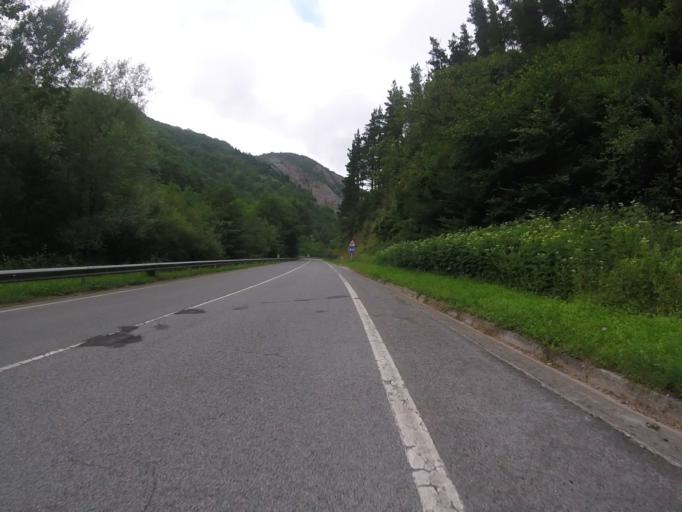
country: ES
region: Navarre
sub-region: Provincia de Navarra
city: Saldias
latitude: 43.1047
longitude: -1.7668
